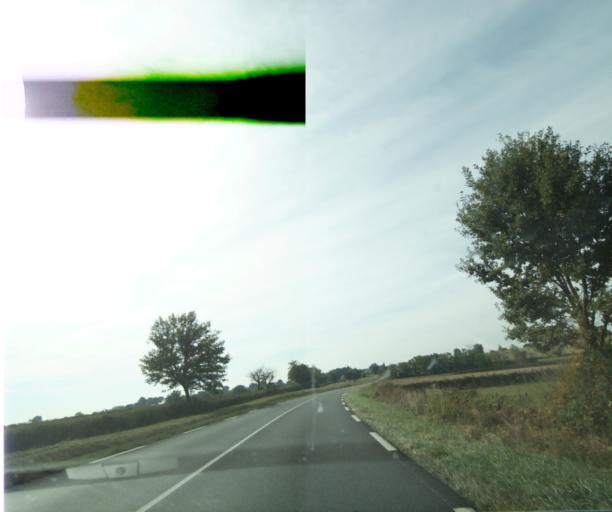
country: FR
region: Auvergne
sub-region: Departement de l'Allier
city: Saint-Francois
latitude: 46.4292
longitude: 3.9097
